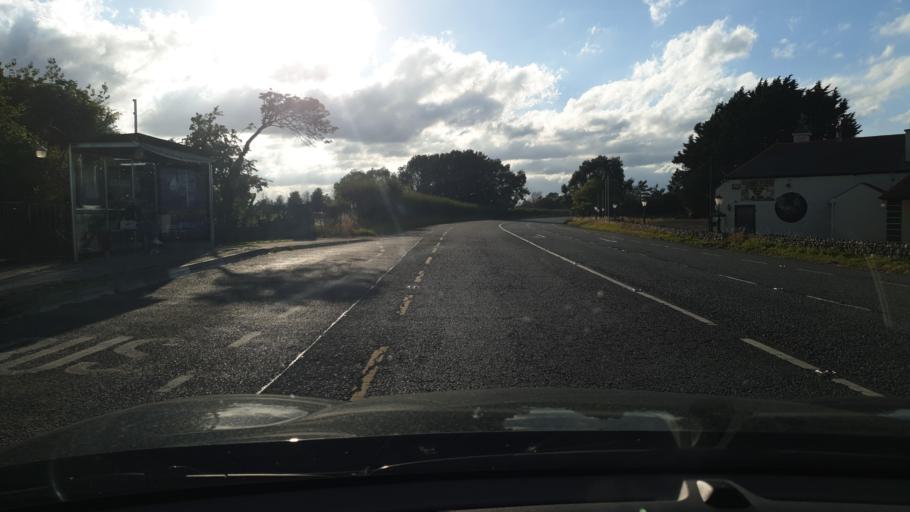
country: IE
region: Leinster
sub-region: An Mhi
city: Stamullin
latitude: 53.6408
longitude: -6.2355
